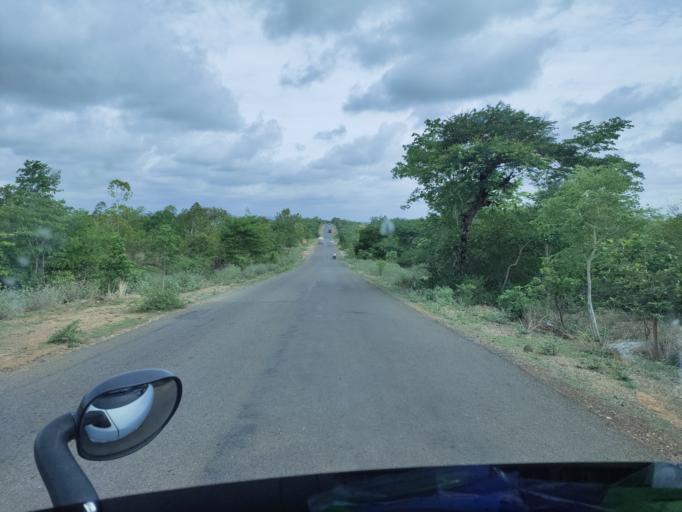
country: MM
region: Magway
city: Chauk
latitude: 20.9712
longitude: 95.0556
